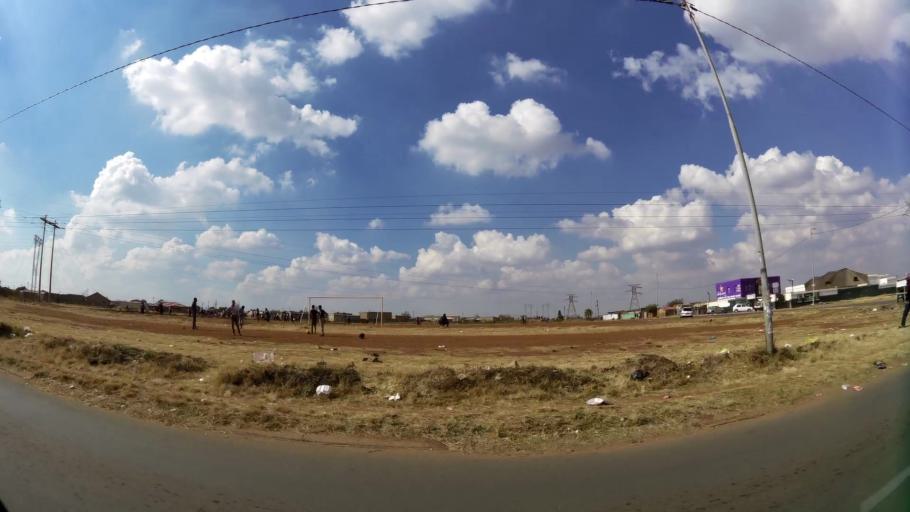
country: ZA
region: Gauteng
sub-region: City of Johannesburg Metropolitan Municipality
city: Roodepoort
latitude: -26.1900
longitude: 27.8561
